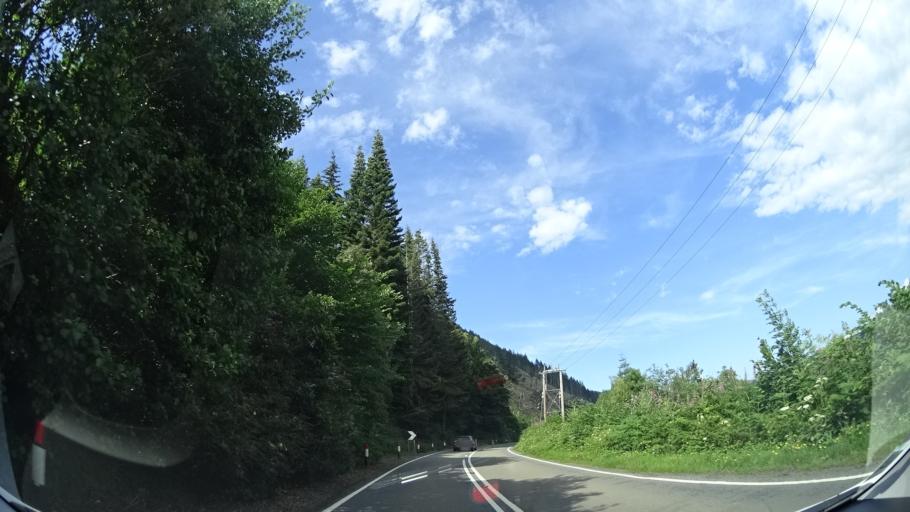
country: GB
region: Scotland
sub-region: Highland
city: Beauly
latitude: 57.2496
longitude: -4.5352
